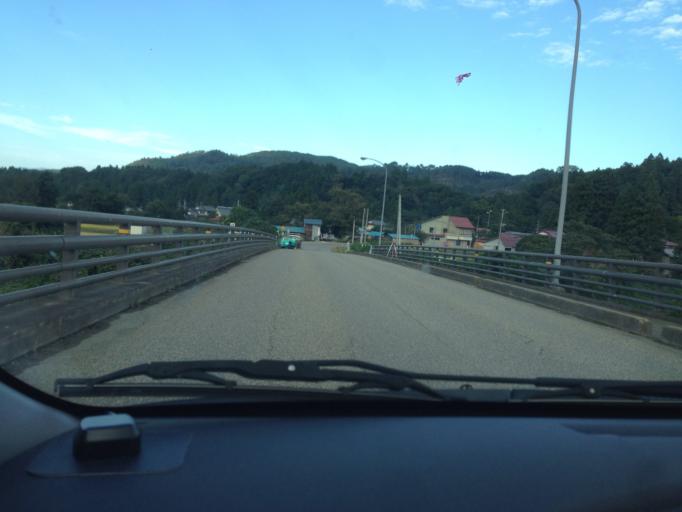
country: JP
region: Fukushima
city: Kitakata
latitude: 37.5765
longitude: 139.7662
